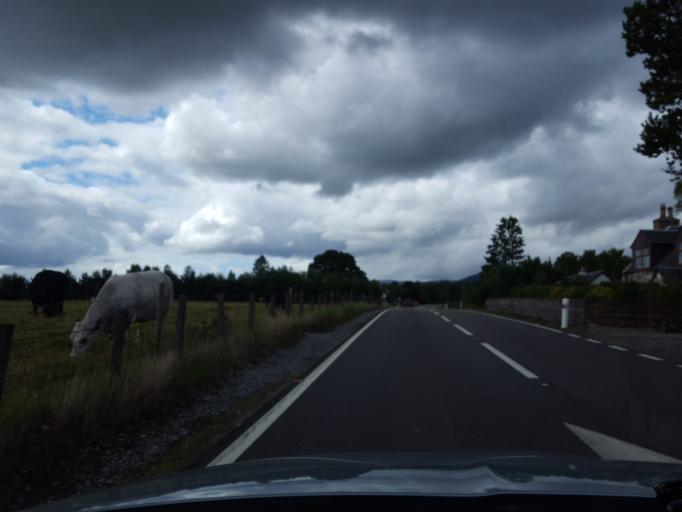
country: GB
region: Scotland
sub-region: Highland
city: Aviemore
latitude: 57.2621
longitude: -3.7393
